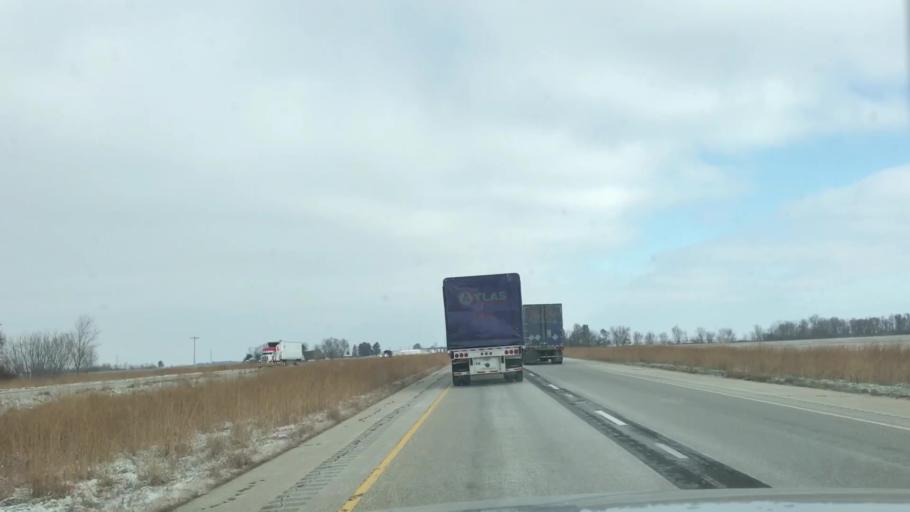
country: US
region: Illinois
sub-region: Sangamon County
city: Divernon
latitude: 39.5137
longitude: -89.6453
